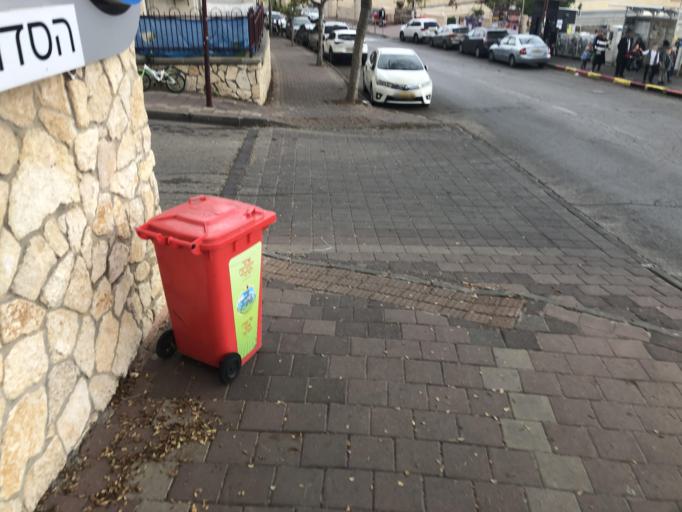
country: IL
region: Jerusalem
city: Modiin Ilit
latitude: 31.9374
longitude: 35.0392
